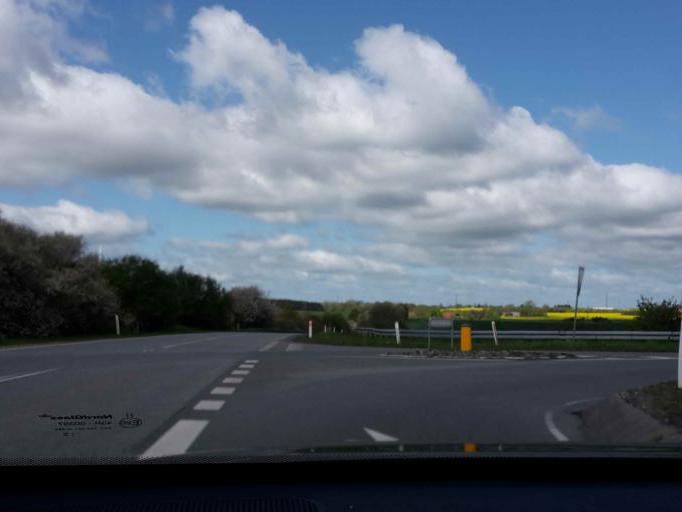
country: DK
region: Central Jutland
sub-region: Arhus Kommune
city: Logten
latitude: 56.2881
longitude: 10.3123
